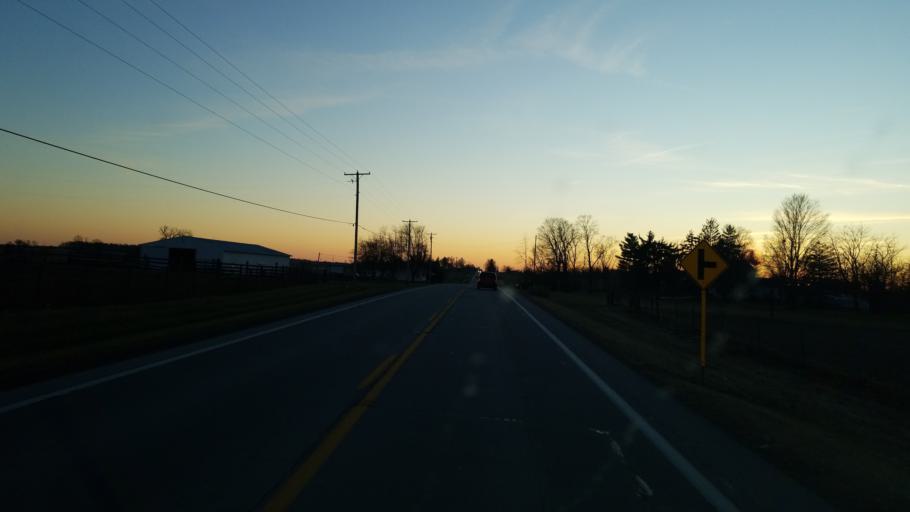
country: US
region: Ohio
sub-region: Fayette County
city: Washington Court House
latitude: 39.6079
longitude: -83.3713
